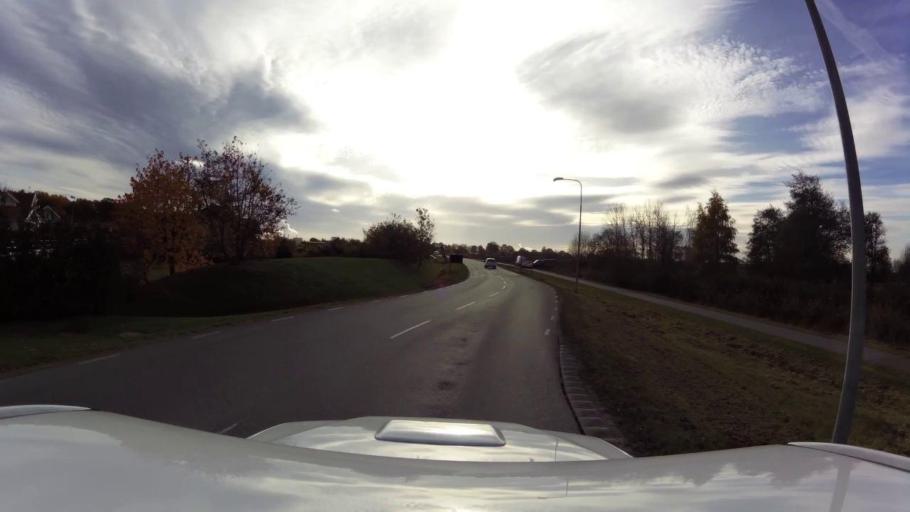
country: SE
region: OEstergoetland
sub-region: Linkopings Kommun
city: Ekangen
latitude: 58.4596
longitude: 15.6401
